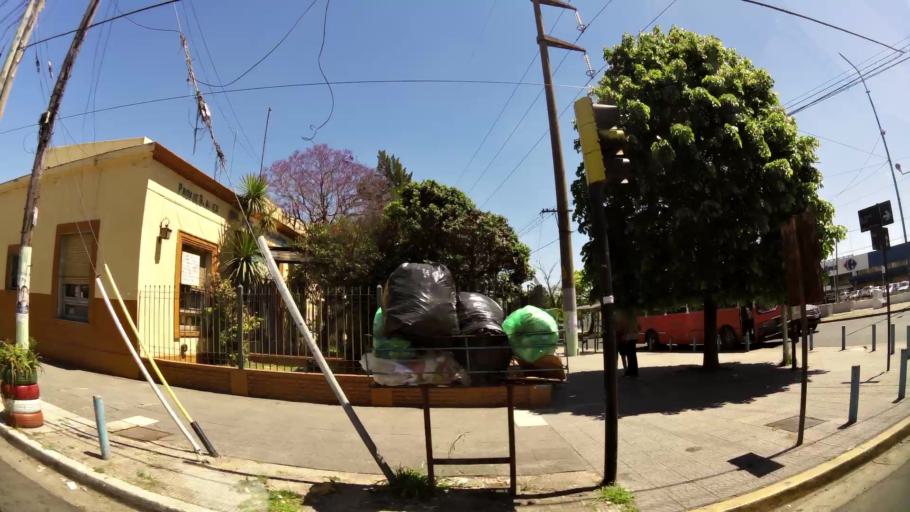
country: AR
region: Buenos Aires
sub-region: Partido de Quilmes
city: Quilmes
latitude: -34.7156
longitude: -58.2984
